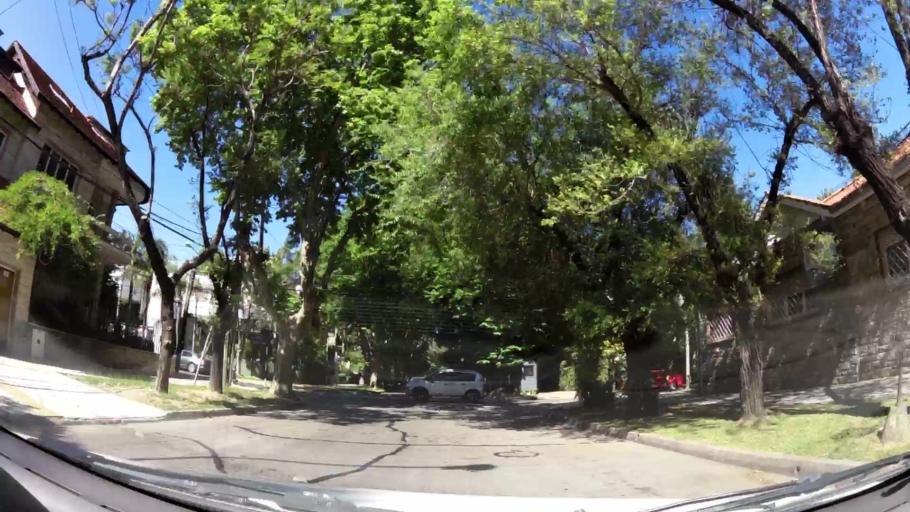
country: AR
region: Buenos Aires
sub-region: Partido de Vicente Lopez
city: Olivos
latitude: -34.5189
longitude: -58.4814
